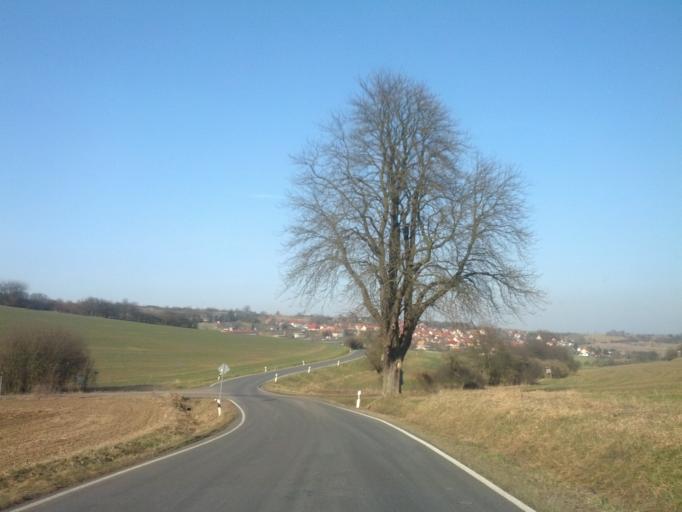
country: DE
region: Thuringia
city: Creuzburg
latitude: 51.0814
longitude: 10.2371
